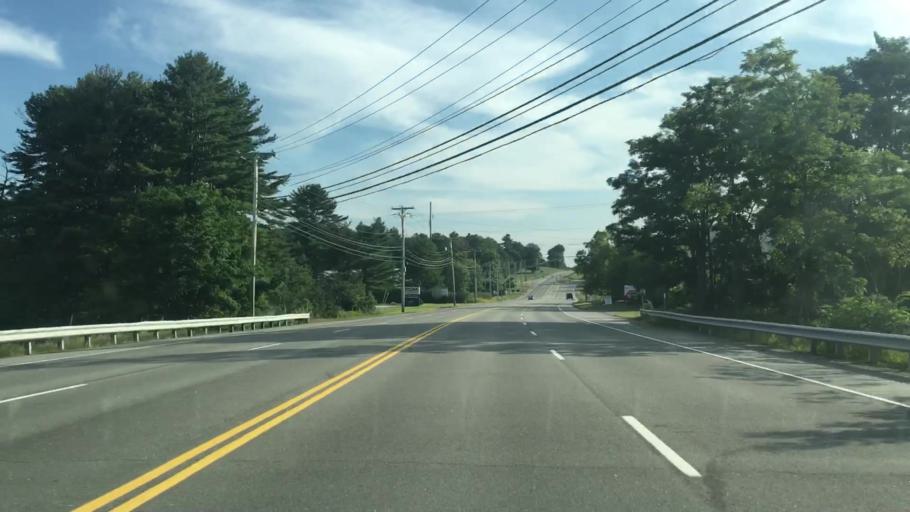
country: US
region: Maine
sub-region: Cumberland County
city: South Portland Gardens
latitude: 43.6089
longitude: -70.3137
